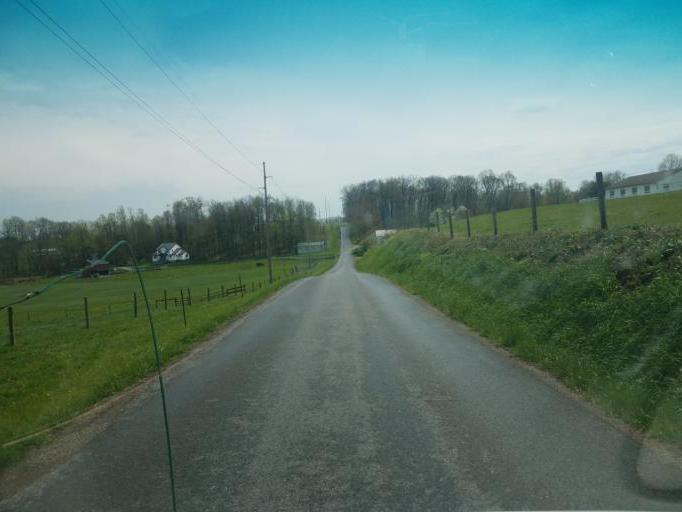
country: US
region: Ohio
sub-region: Holmes County
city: Millersburg
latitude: 40.5477
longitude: -81.8500
